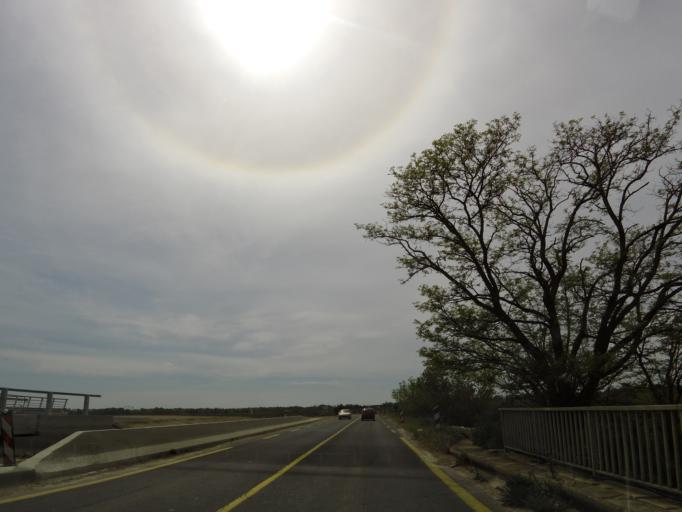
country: FR
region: Languedoc-Roussillon
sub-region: Departement de l'Herault
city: La Grande-Motte
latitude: 43.5850
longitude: 4.1042
